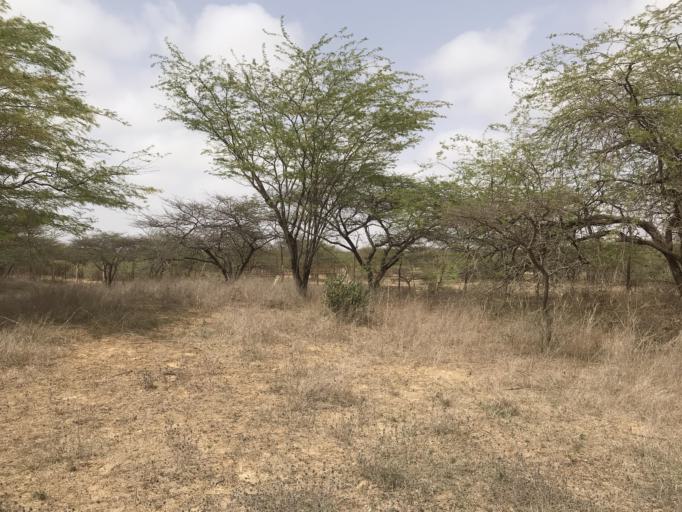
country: SN
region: Saint-Louis
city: Saint-Louis
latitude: 15.9207
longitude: -16.4527
